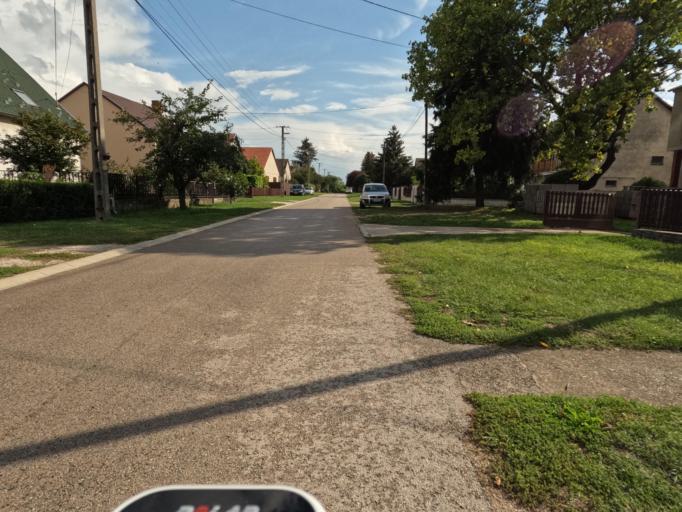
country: HU
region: Tolna
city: Tengelic
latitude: 46.5251
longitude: 18.7110
